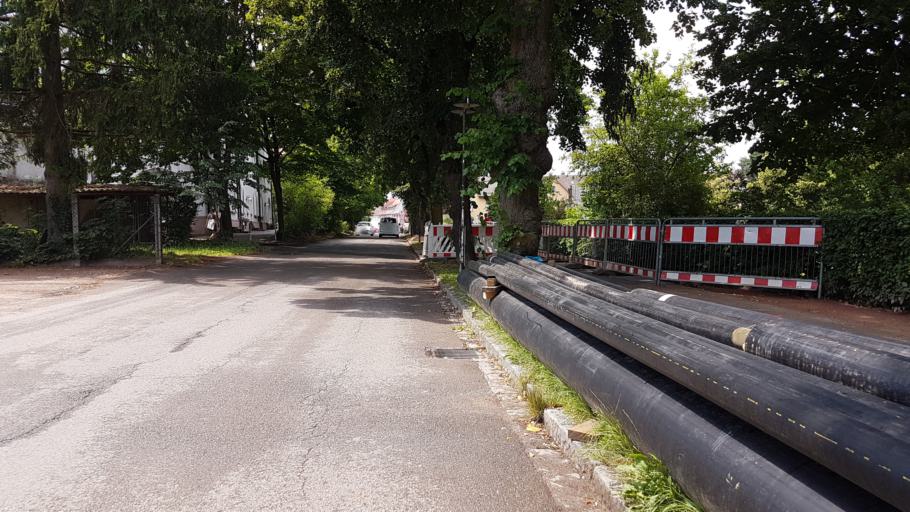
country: DE
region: Baden-Wuerttemberg
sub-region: Freiburg Region
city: Hufingen
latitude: 47.9261
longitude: 8.4920
